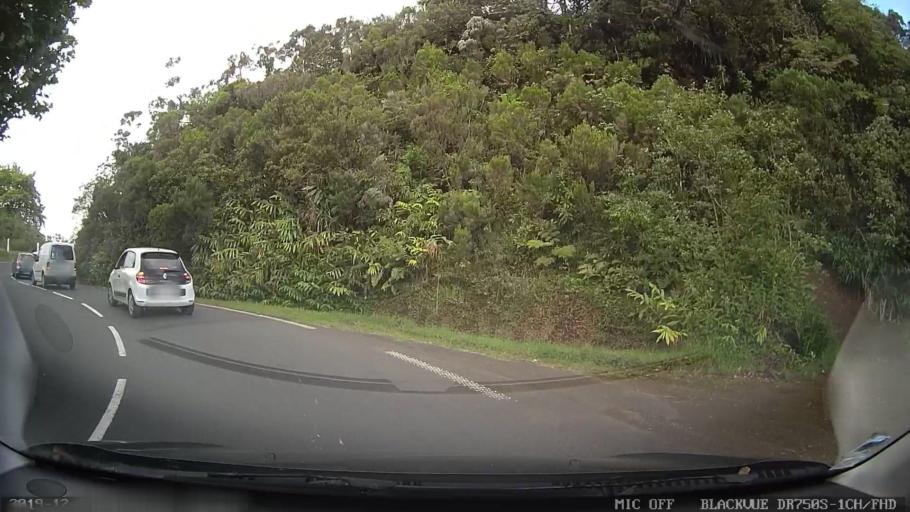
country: RE
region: Reunion
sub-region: Reunion
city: Cilaos
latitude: -21.1614
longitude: 55.5934
